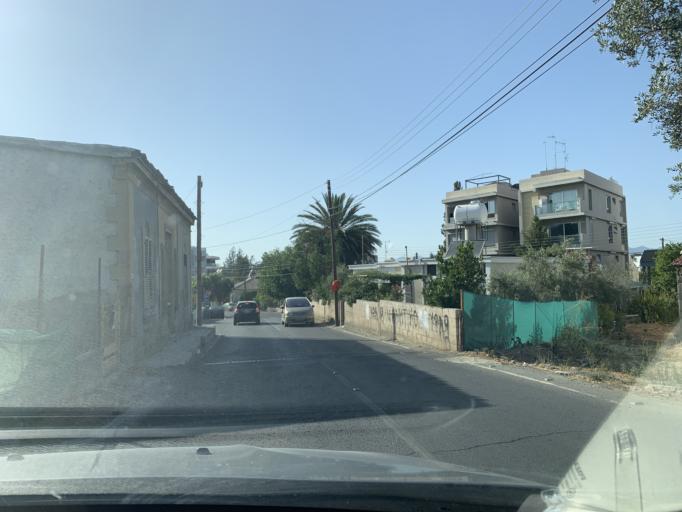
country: CY
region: Lefkosia
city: Nicosia
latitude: 35.1533
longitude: 33.3946
